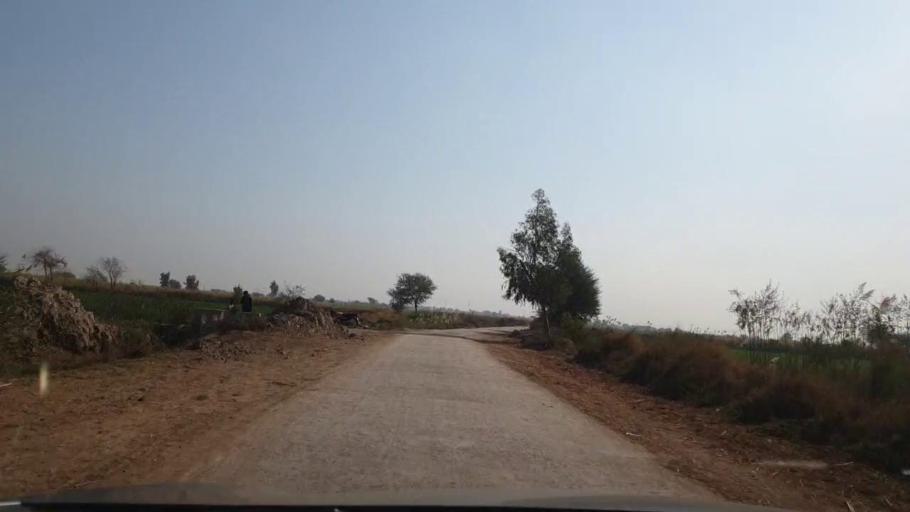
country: PK
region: Sindh
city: Berani
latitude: 25.6464
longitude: 68.8947
